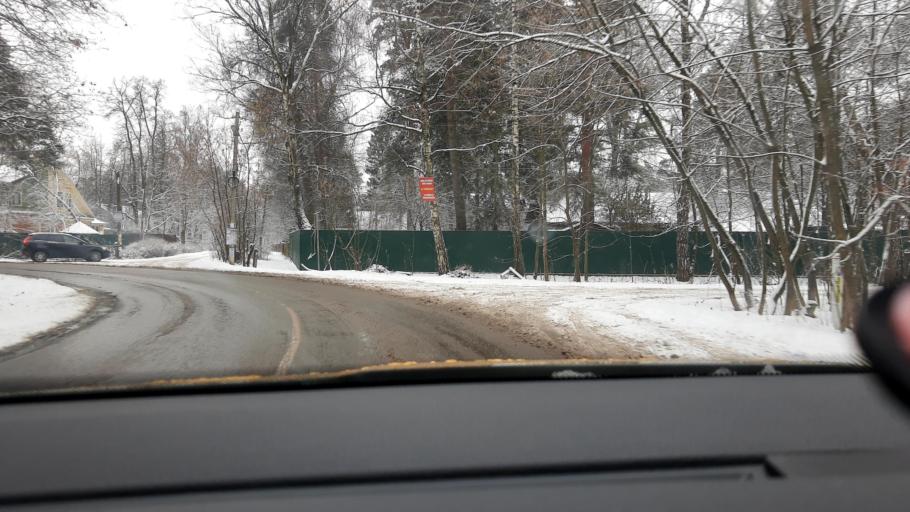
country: RU
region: Moskovskaya
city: Mamontovka
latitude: 55.9747
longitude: 37.8215
